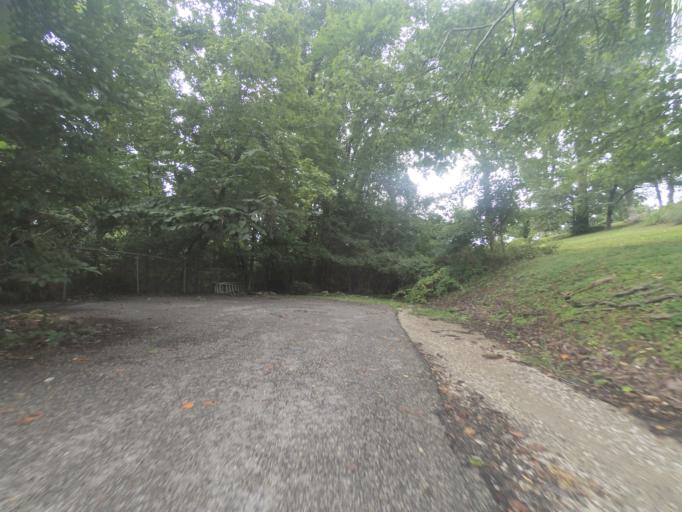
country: US
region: West Virginia
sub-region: Cabell County
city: Huntington
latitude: 38.4040
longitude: -82.4508
